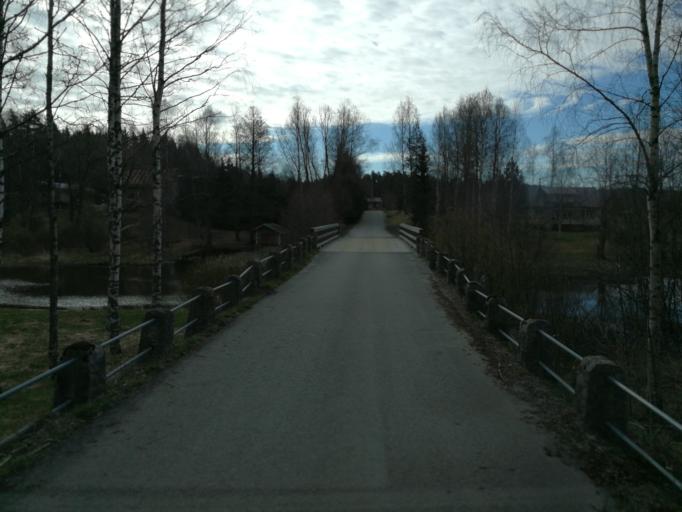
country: FI
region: Varsinais-Suomi
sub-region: Salo
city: Kisko
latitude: 60.2627
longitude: 23.4590
